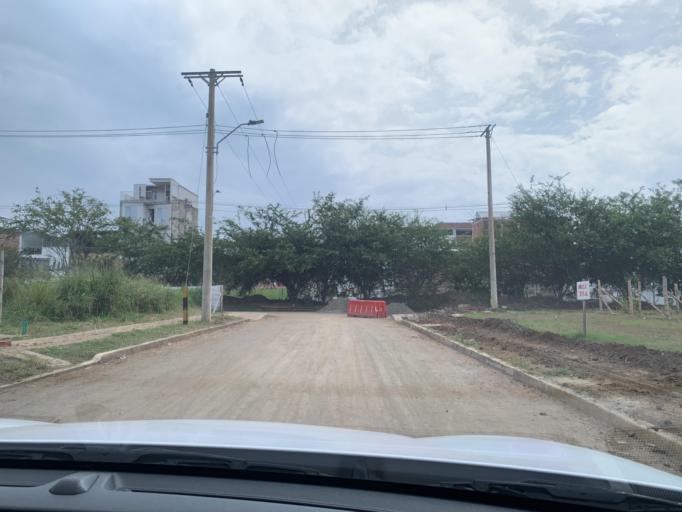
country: CO
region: Valle del Cauca
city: Cali
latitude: 3.3924
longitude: -76.5199
